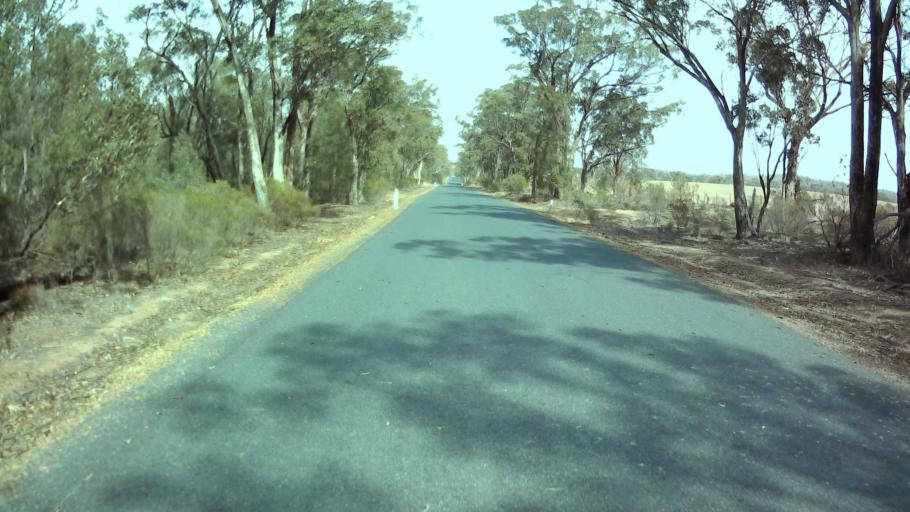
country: AU
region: New South Wales
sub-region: Weddin
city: Grenfell
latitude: -33.8032
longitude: 148.0242
